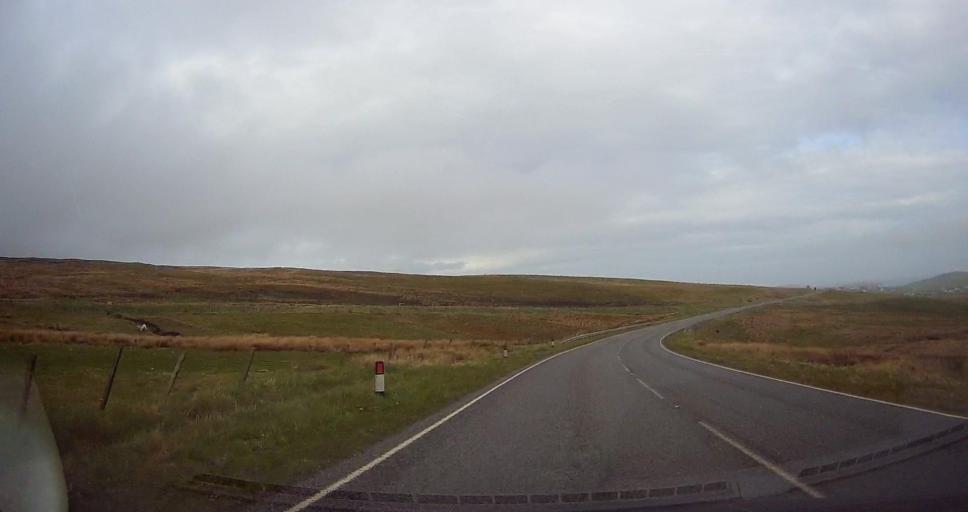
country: GB
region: Scotland
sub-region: Shetland Islands
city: Sandwick
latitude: 60.0105
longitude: -1.2615
